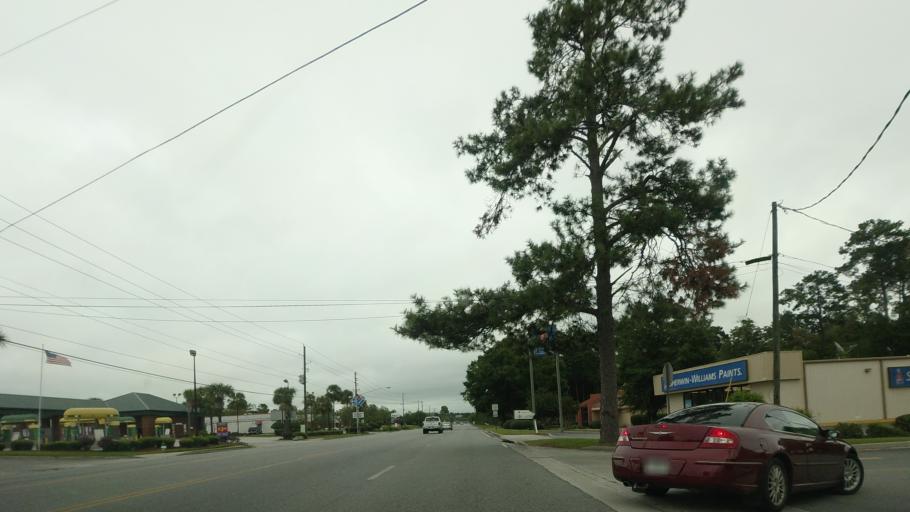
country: US
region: Georgia
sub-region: Lowndes County
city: Remerton
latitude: 30.8696
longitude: -83.2873
